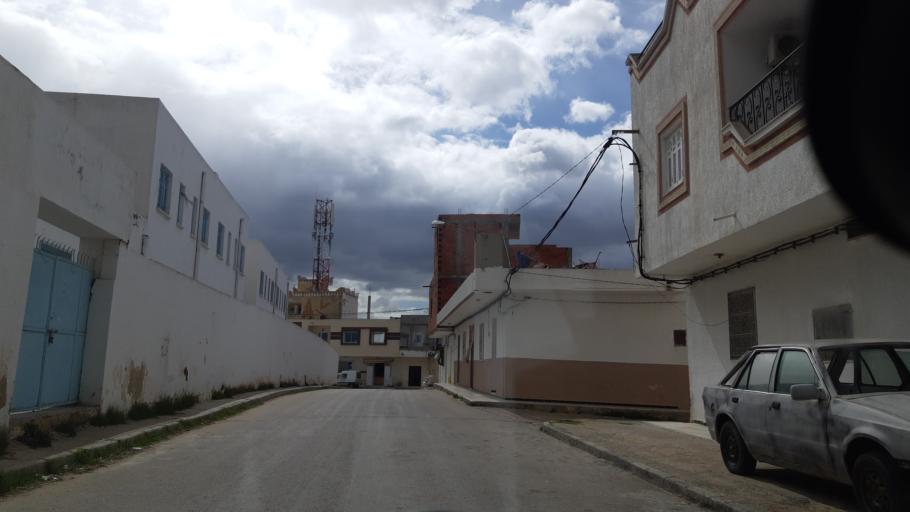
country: TN
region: Susah
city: Akouda
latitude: 35.8692
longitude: 10.5247
